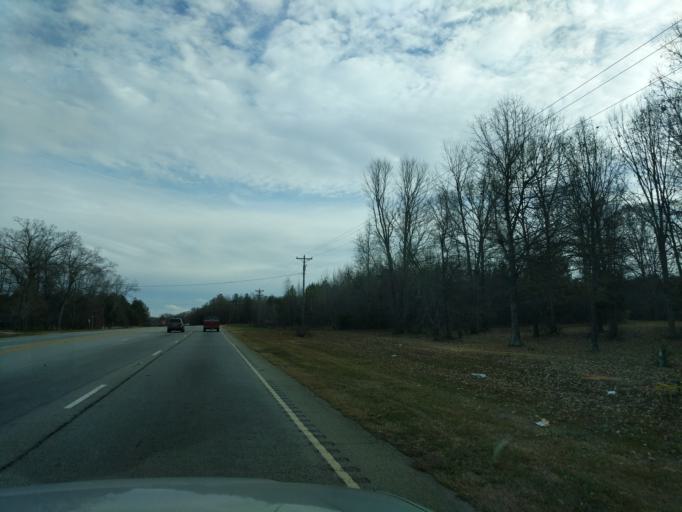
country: US
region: South Carolina
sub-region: Anderson County
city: Williamston
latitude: 34.6183
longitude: -82.3813
